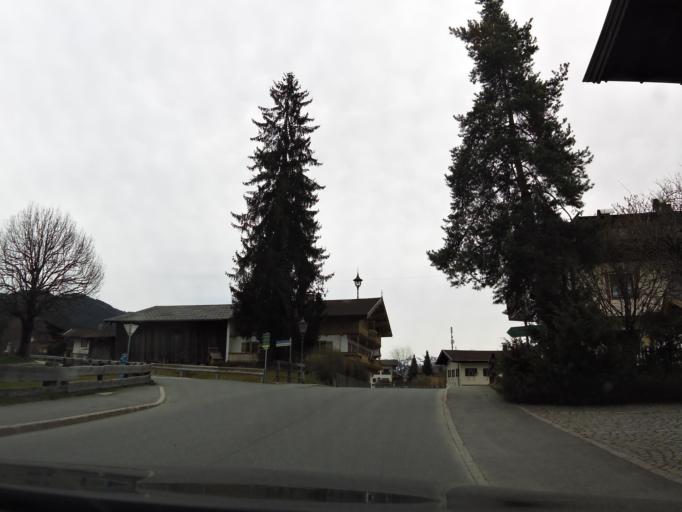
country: AT
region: Tyrol
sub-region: Politischer Bezirk Kitzbuhel
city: Brixen im Thale
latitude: 47.4497
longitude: 12.2585
